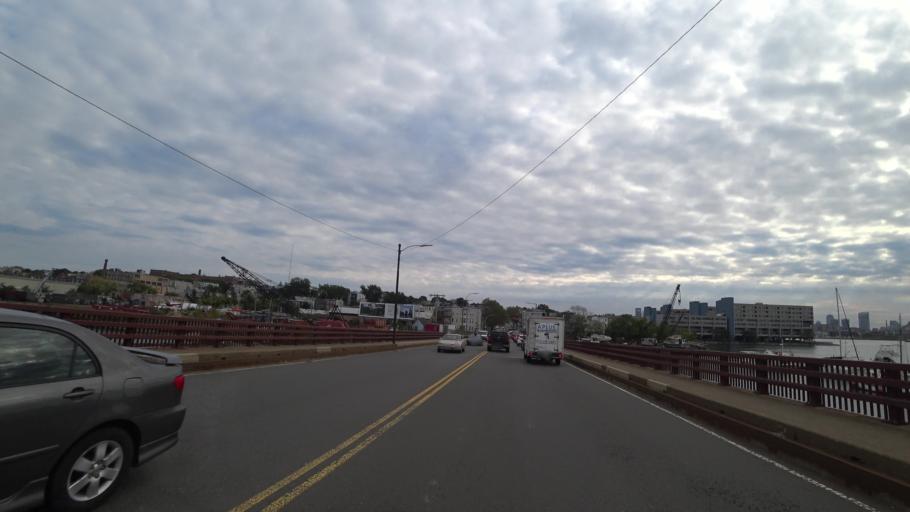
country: US
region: Massachusetts
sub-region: Suffolk County
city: Chelsea
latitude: 42.3846
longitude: -71.0393
